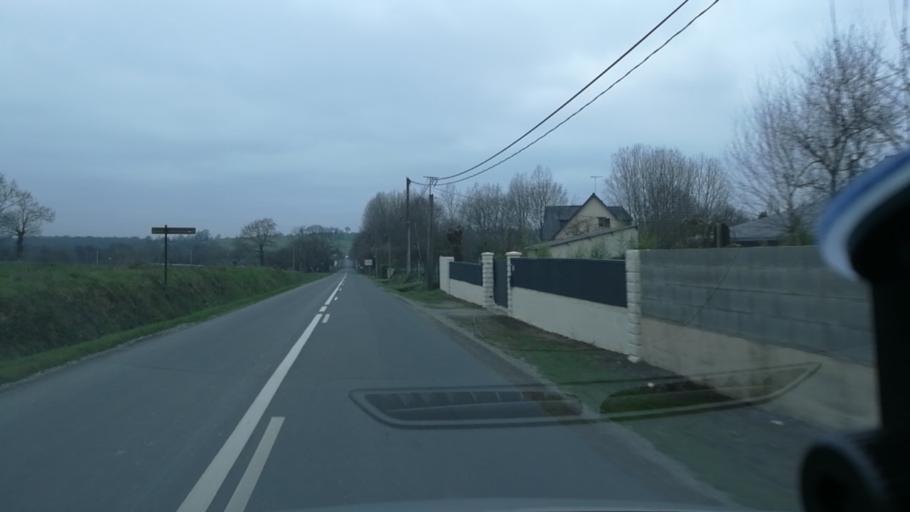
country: FR
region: Brittany
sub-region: Departement d'Ille-et-Vilaine
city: Tresboeuf
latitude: 47.8817
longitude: -1.4967
